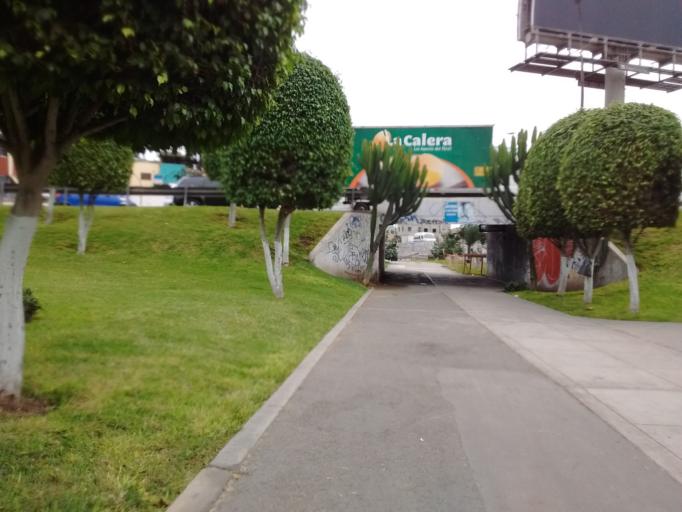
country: PE
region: Callao
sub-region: Callao
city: Callao
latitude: -12.0539
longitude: -77.0976
